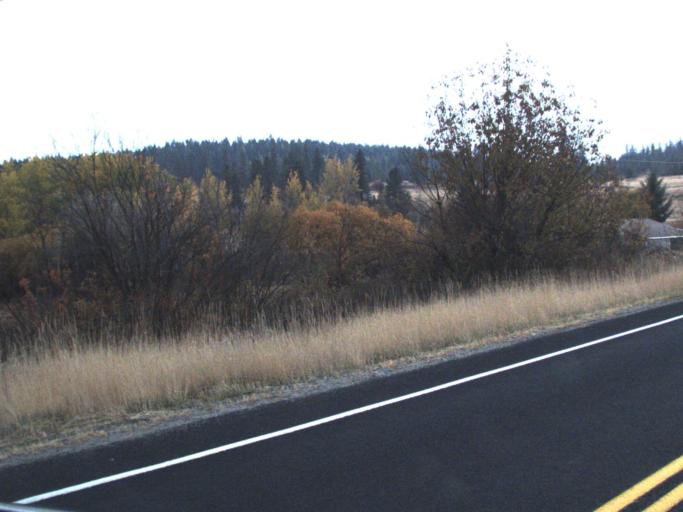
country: US
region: Washington
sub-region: Lincoln County
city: Davenport
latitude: 47.9939
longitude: -118.2846
